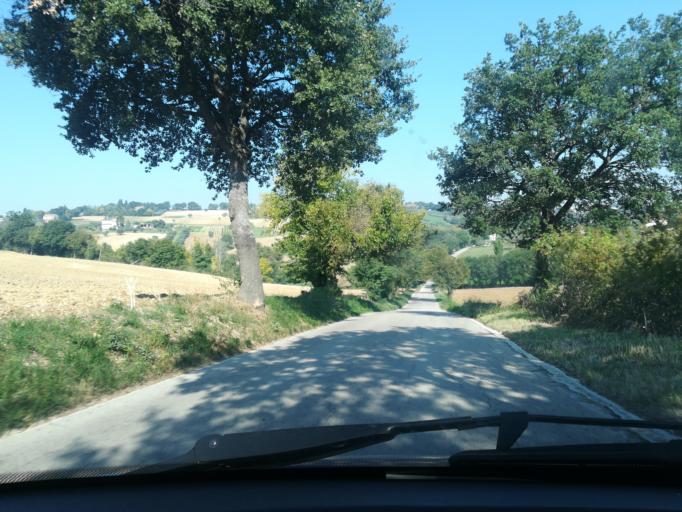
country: IT
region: The Marches
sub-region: Provincia di Macerata
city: Macerata
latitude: 43.2707
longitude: 13.4507
